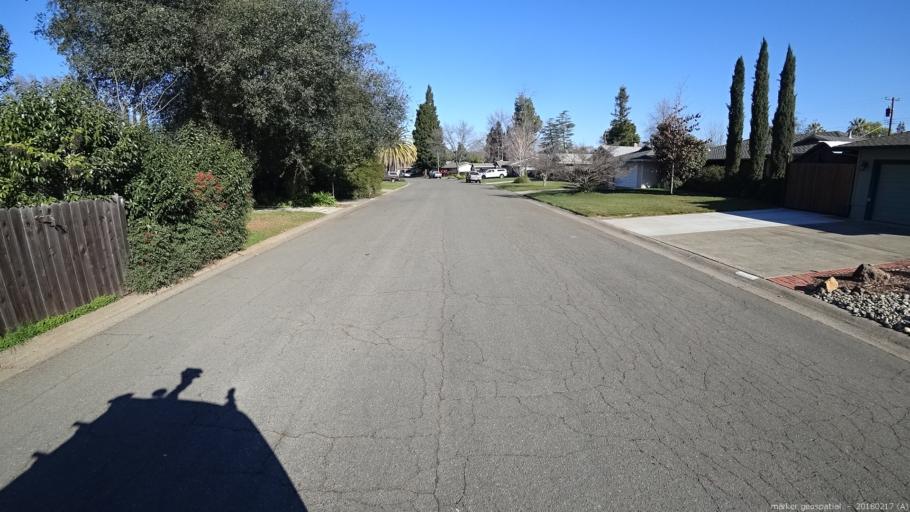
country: US
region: California
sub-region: Sacramento County
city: Folsom
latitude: 38.6634
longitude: -121.1980
